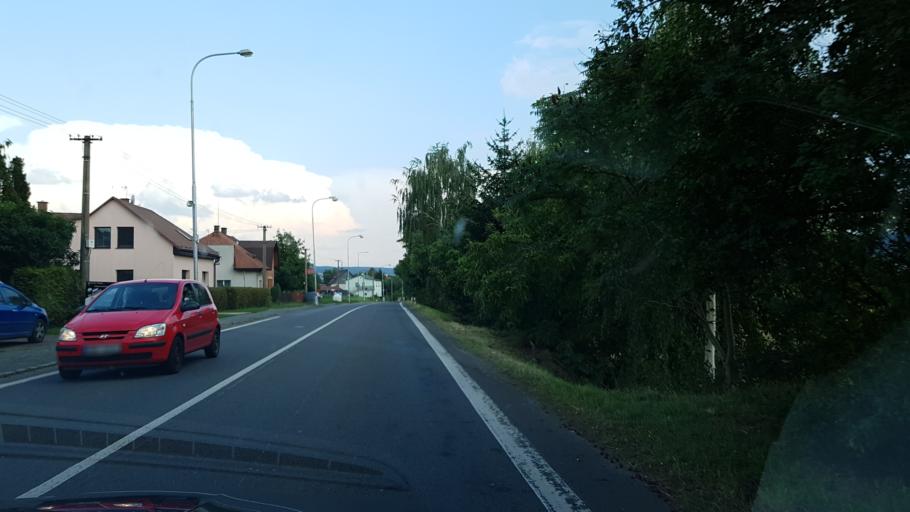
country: CZ
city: Doudleby nad Orlici
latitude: 50.1126
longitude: 16.2503
